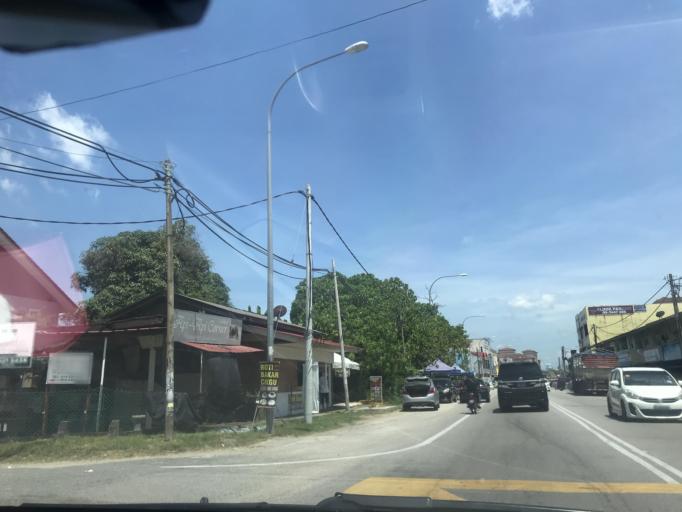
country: MY
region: Kelantan
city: Kota Bharu
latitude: 6.1247
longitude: 102.2509
